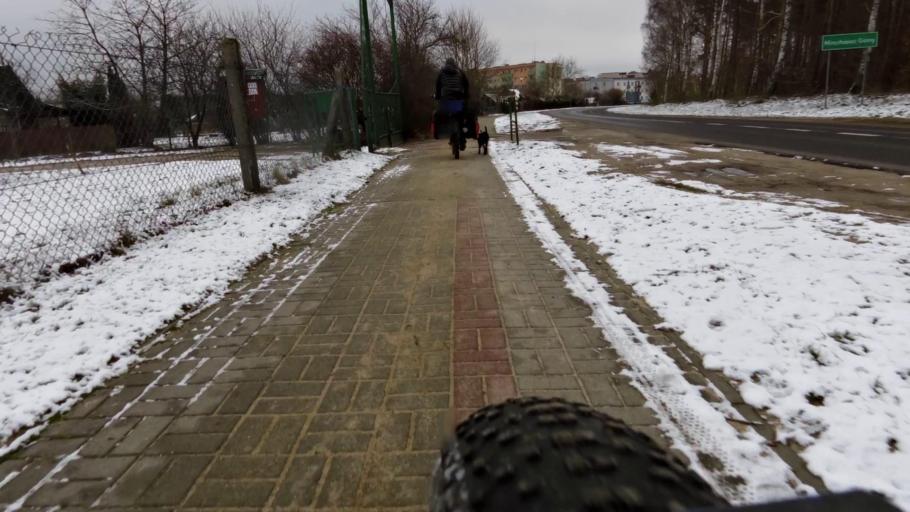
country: PL
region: West Pomeranian Voivodeship
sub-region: Powiat walecki
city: Miroslawiec
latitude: 53.3690
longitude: 16.0845
